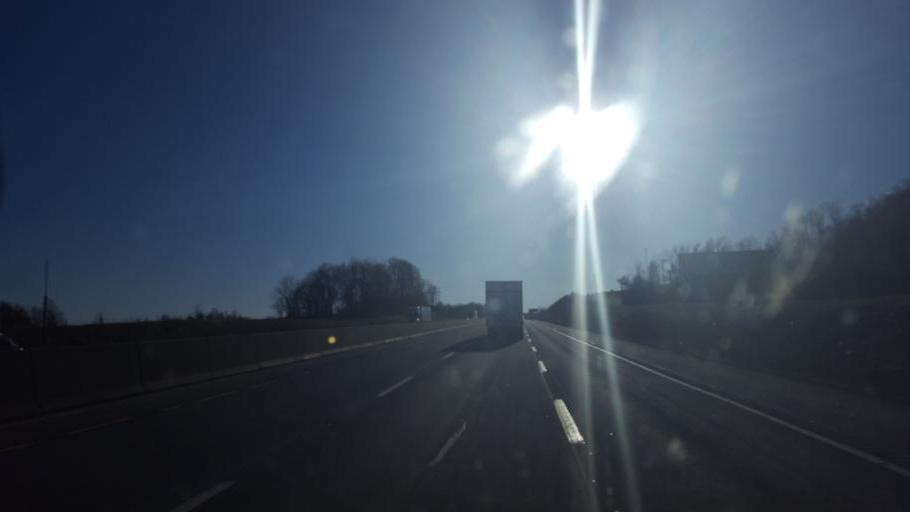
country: US
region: Pennsylvania
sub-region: Fayette County
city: Bear Rocks
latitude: 40.1175
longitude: -79.3392
